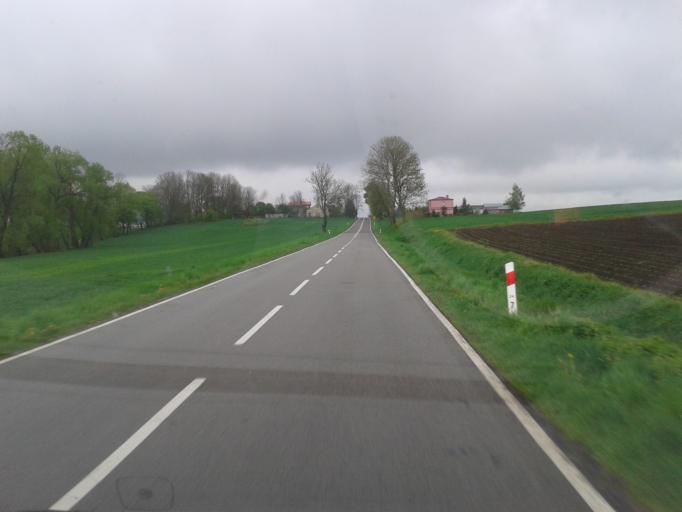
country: PL
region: Lublin Voivodeship
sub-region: Powiat hrubieszowski
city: Dolhobyczow
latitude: 50.5817
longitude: 23.9684
